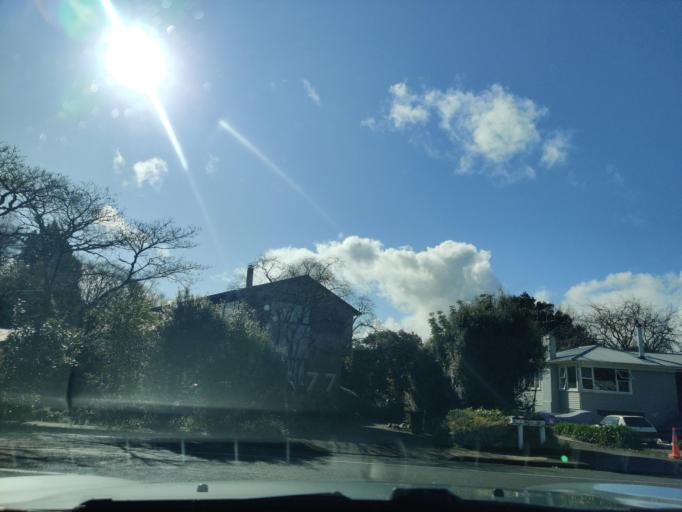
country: NZ
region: Hawke's Bay
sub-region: Hastings District
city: Hastings
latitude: -39.6751
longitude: 176.8880
